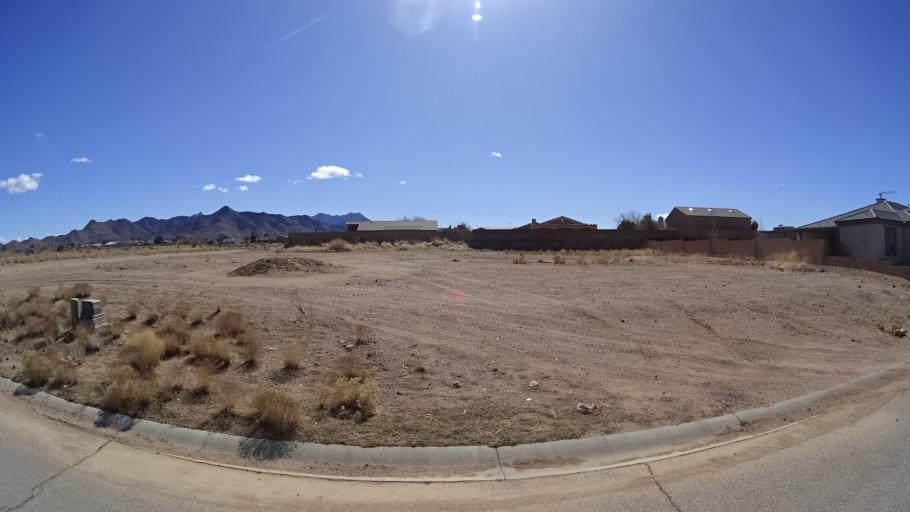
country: US
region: Arizona
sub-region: Mohave County
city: Kingman
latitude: 35.2067
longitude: -113.9681
